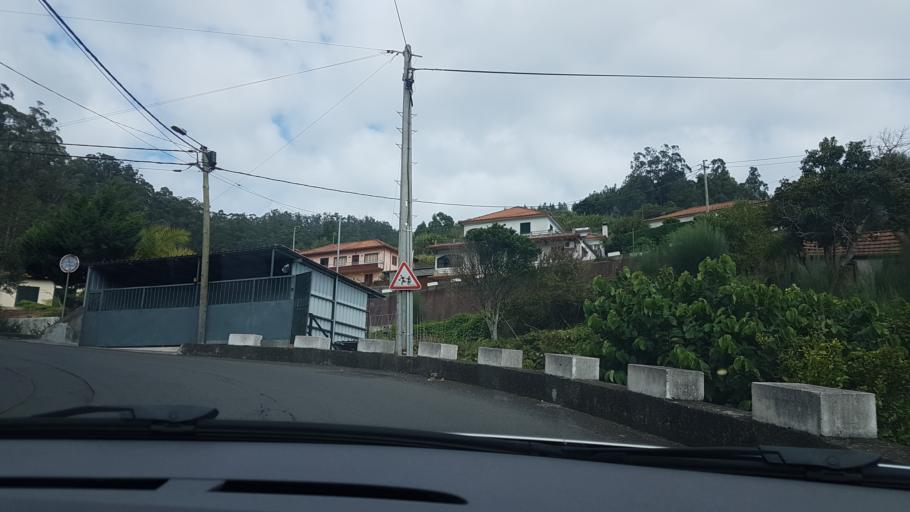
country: PT
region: Madeira
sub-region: Santa Cruz
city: Santa Cruz
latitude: 32.7366
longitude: -16.8168
